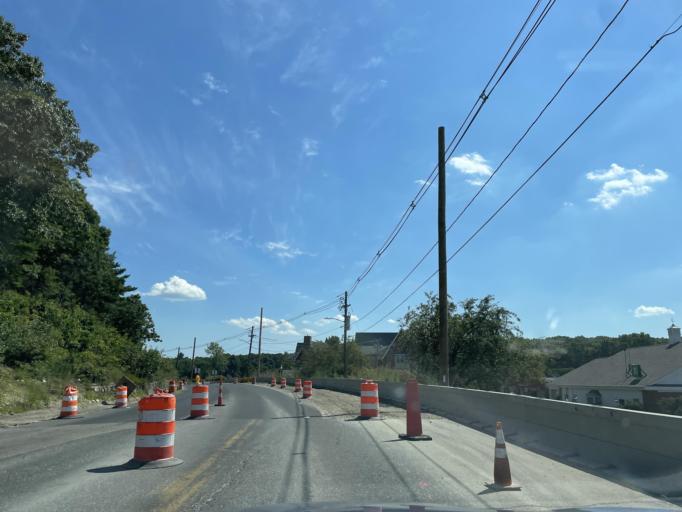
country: US
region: Massachusetts
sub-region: Middlesex County
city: Ashland
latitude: 42.2396
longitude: -71.4325
